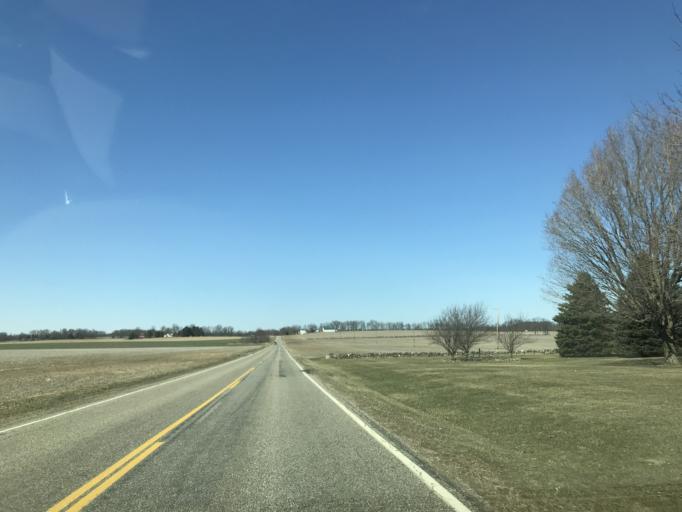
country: US
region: Michigan
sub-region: Hillsdale County
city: Jonesville
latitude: 41.9855
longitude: -84.7152
